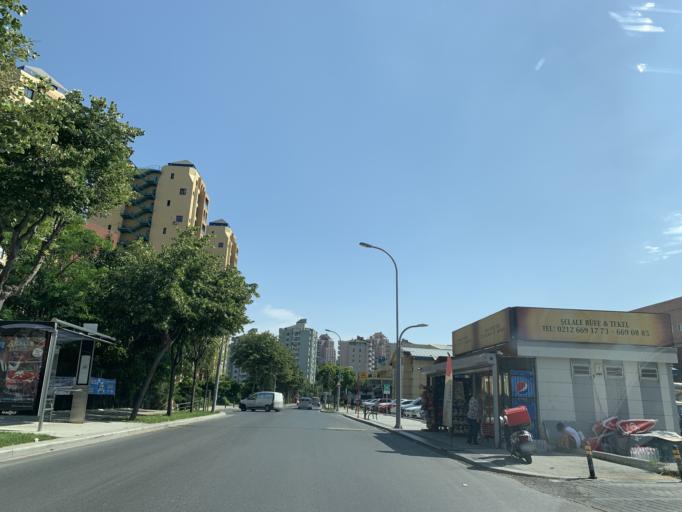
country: TR
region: Istanbul
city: Esenyurt
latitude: 41.0694
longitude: 28.6780
